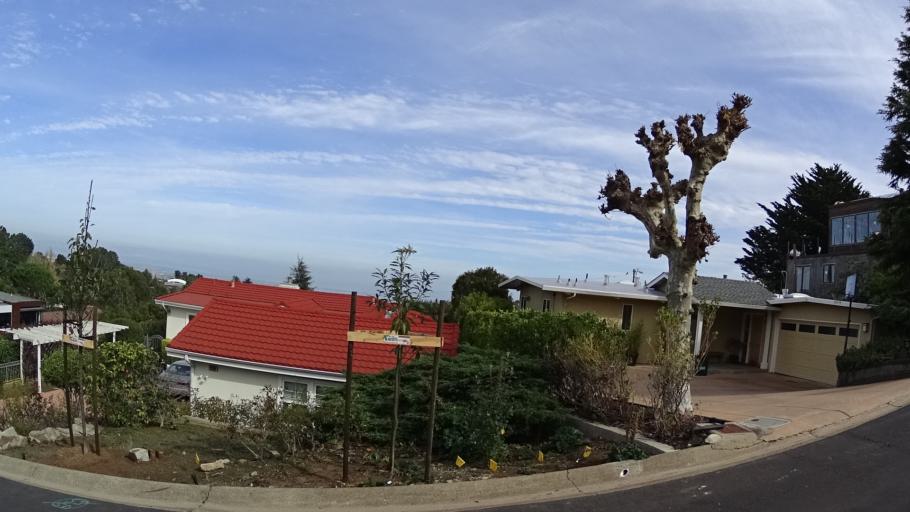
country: US
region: California
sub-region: San Mateo County
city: Hillsborough
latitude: 37.5761
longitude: -122.3964
